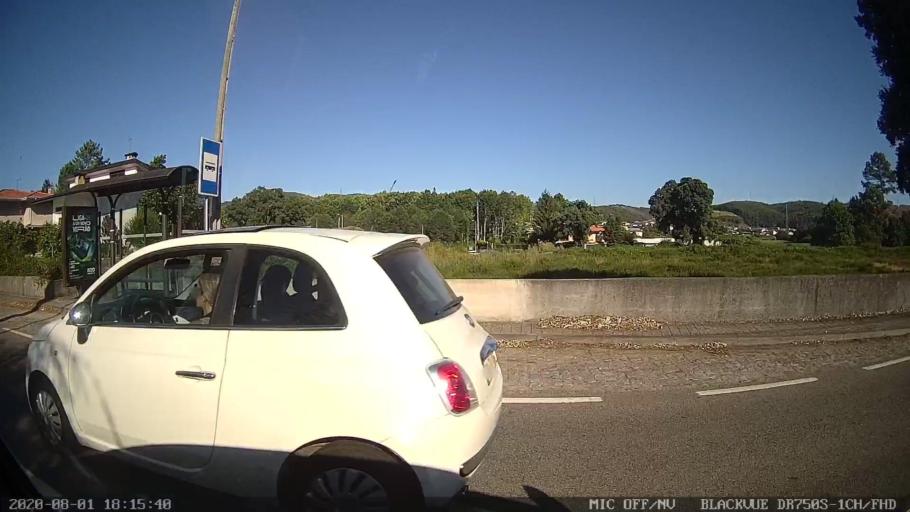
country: PT
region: Porto
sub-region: Valongo
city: Alfena
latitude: 41.2629
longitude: -8.4813
